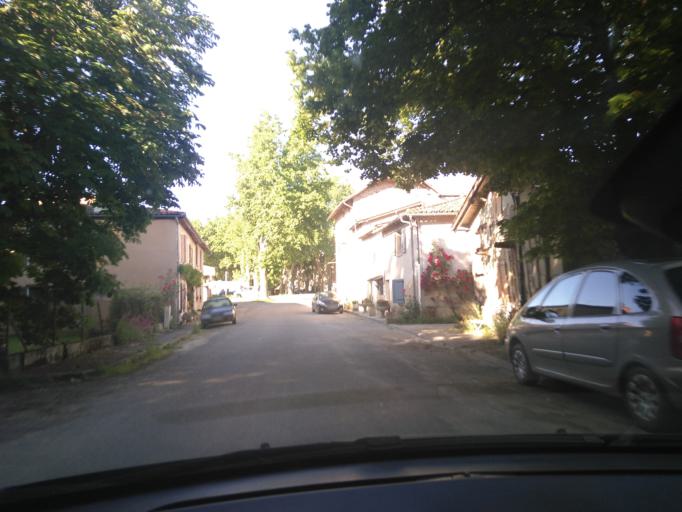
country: FR
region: Midi-Pyrenees
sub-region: Departement du Tarn-et-Garonne
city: Beaumont-de-Lomagne
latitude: 43.7749
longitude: 0.9302
